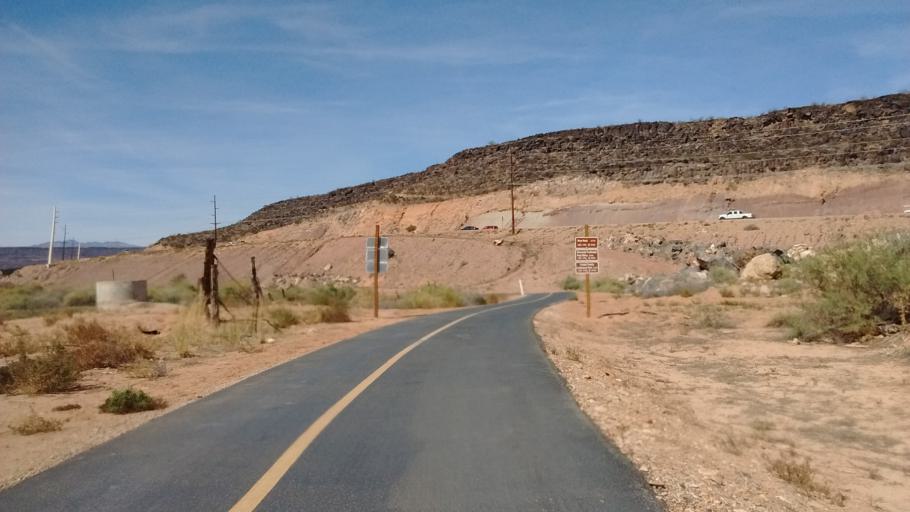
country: US
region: Utah
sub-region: Washington County
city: Saint George
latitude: 37.0873
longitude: -113.5456
